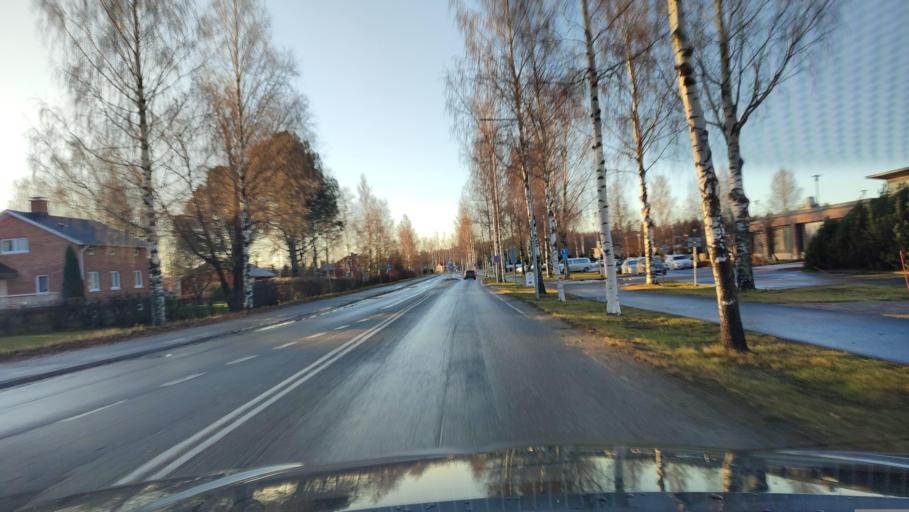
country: FI
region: Ostrobothnia
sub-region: Sydosterbotten
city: Naerpes
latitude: 62.4723
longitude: 21.3366
